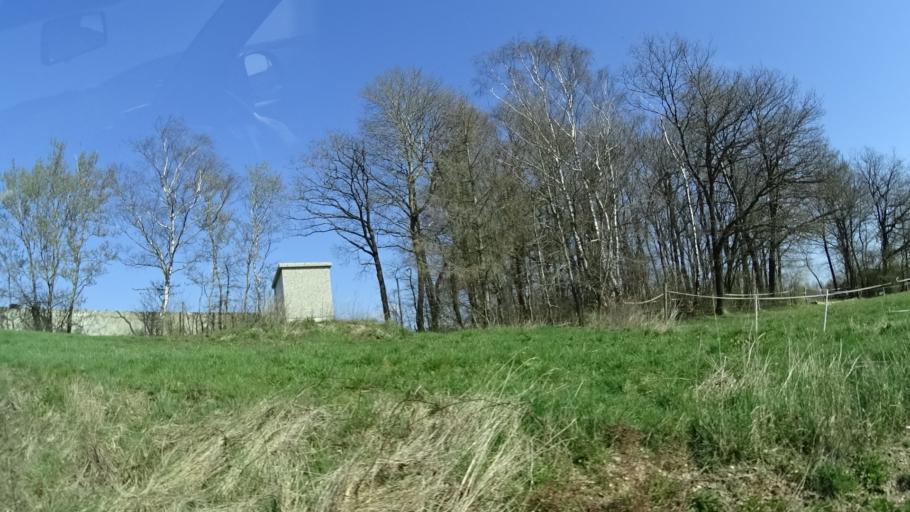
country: DE
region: Rheinland-Pfalz
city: Schwollen
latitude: 49.6969
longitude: 7.1717
